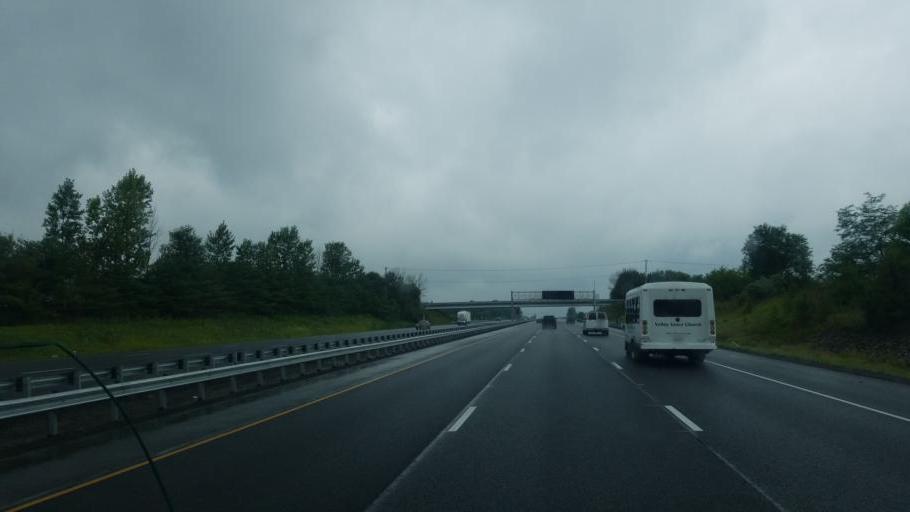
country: US
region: Indiana
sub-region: Madison County
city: Ingalls
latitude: 39.9919
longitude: -85.7934
